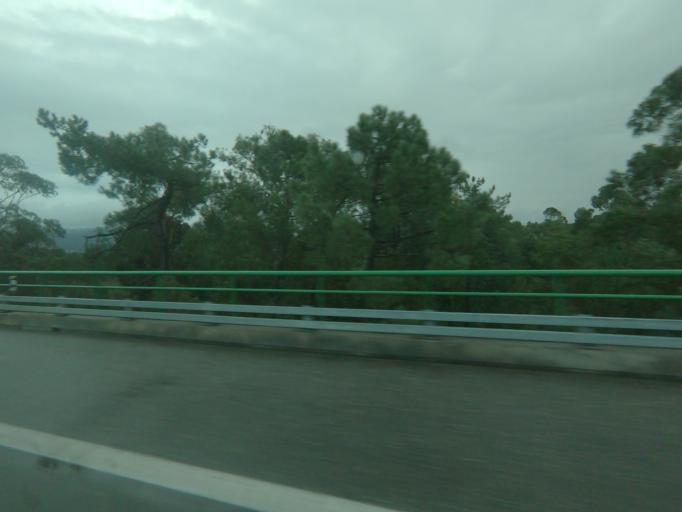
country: PT
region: Viana do Castelo
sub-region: Valenca
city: Valenza
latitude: 41.9733
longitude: -8.6619
